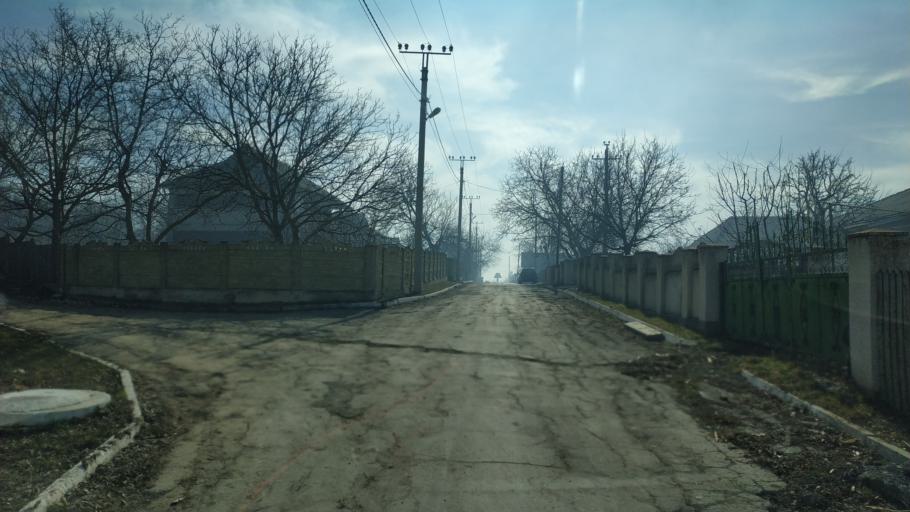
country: MD
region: Nisporeni
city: Nisporeni
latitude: 47.0747
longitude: 28.2642
